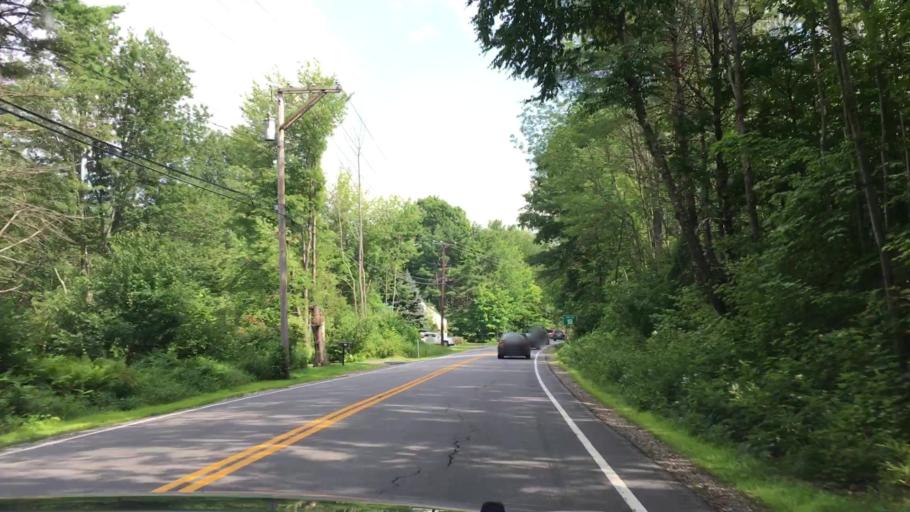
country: US
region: New Hampshire
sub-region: Belknap County
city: Gilford
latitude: 43.5910
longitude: -71.4236
